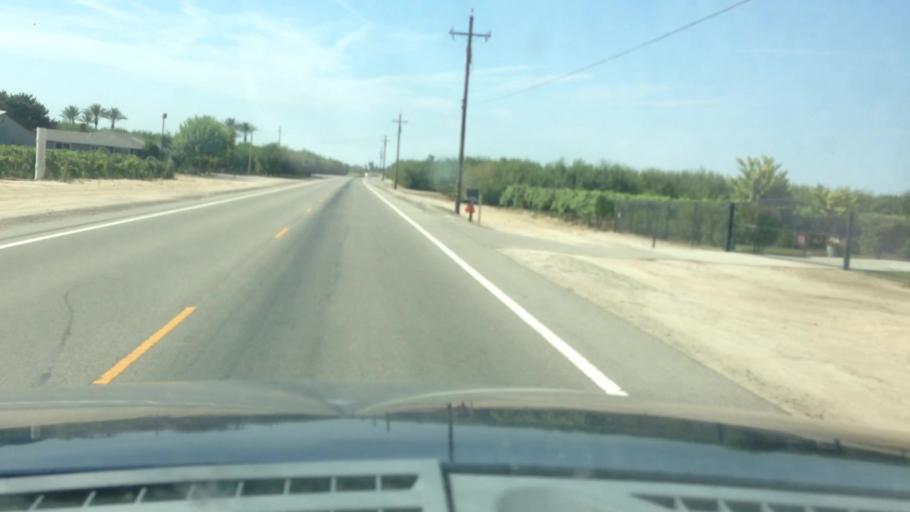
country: US
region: California
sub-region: Fresno County
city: Parlier
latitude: 36.5878
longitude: -119.5570
